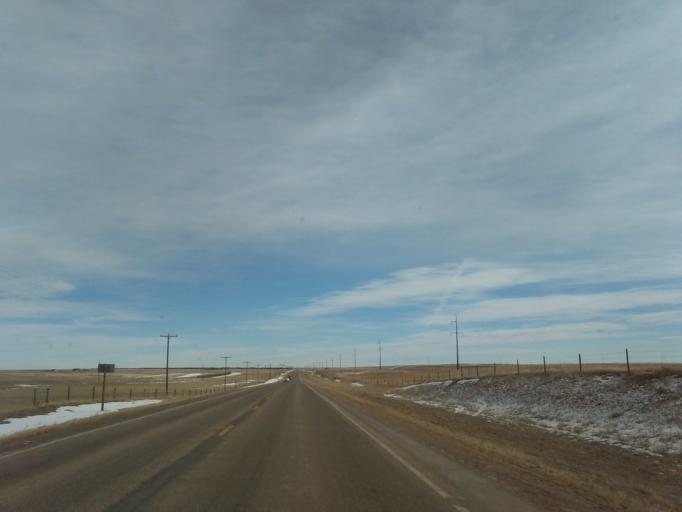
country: US
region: Wyoming
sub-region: Laramie County
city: Ranchettes
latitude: 41.4030
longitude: -104.4594
